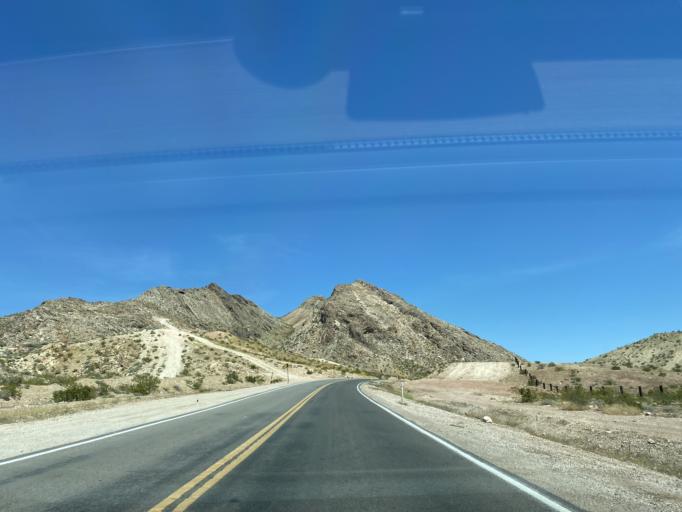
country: US
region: Nevada
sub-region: Clark County
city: Nellis Air Force Base
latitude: 36.2025
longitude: -114.9889
